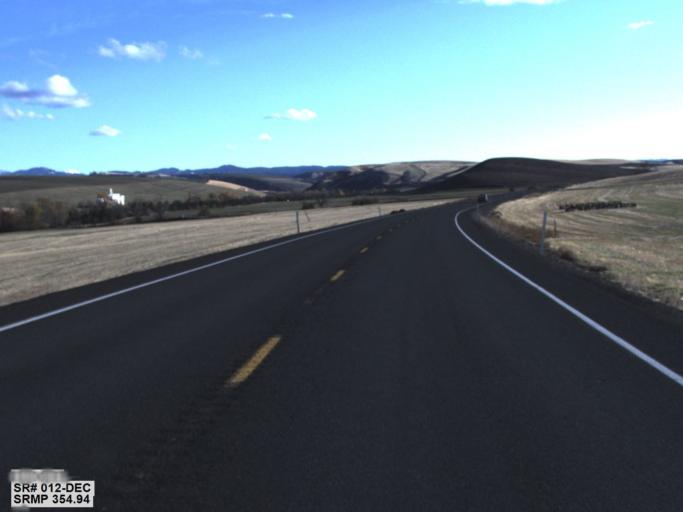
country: US
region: Washington
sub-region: Walla Walla County
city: Waitsburg
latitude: 46.2339
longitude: -118.1388
